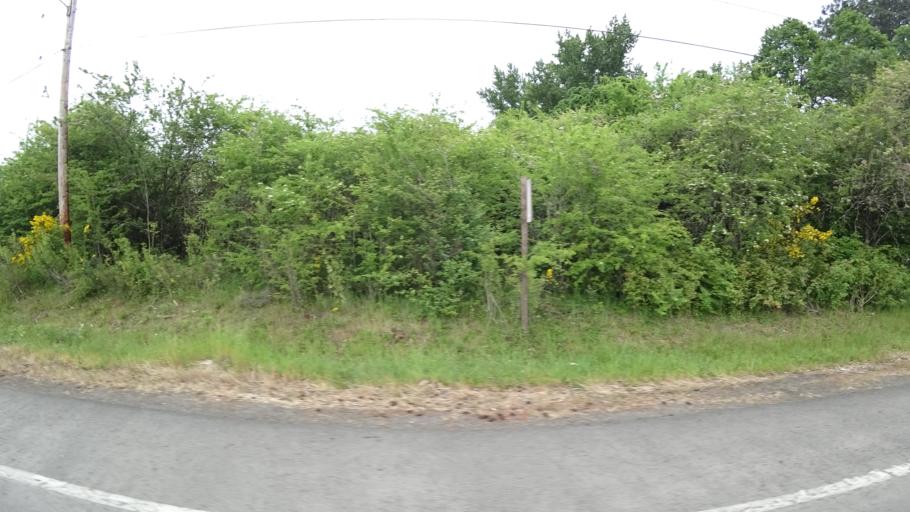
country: US
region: Oregon
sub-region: Washington County
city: Hillsboro
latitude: 45.4802
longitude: -122.9912
